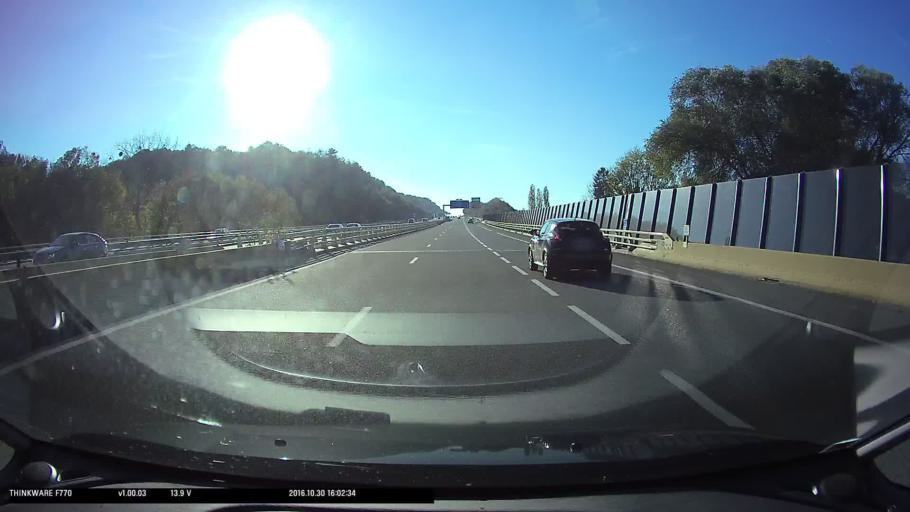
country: FR
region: Franche-Comte
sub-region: Departement du Doubs
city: Arbouans
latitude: 47.4856
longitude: 6.8077
